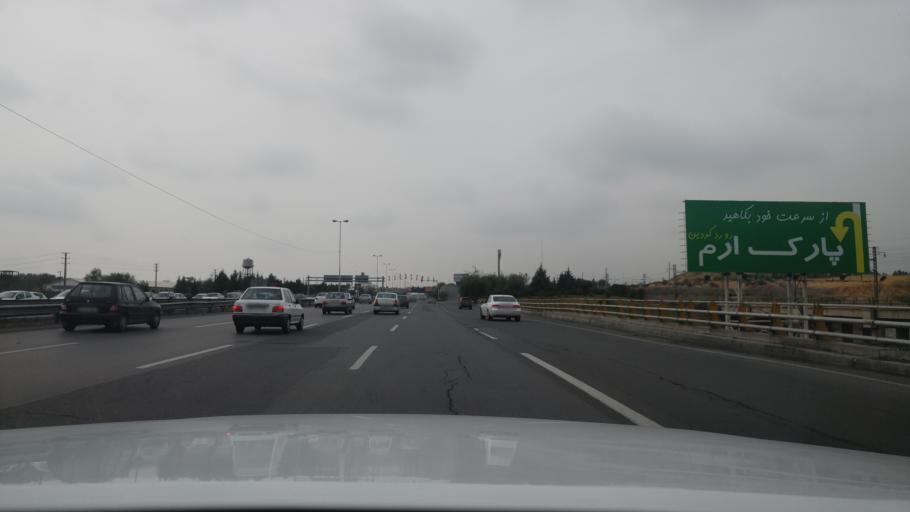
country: IR
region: Tehran
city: Tehran
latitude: 35.7164
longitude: 51.2920
